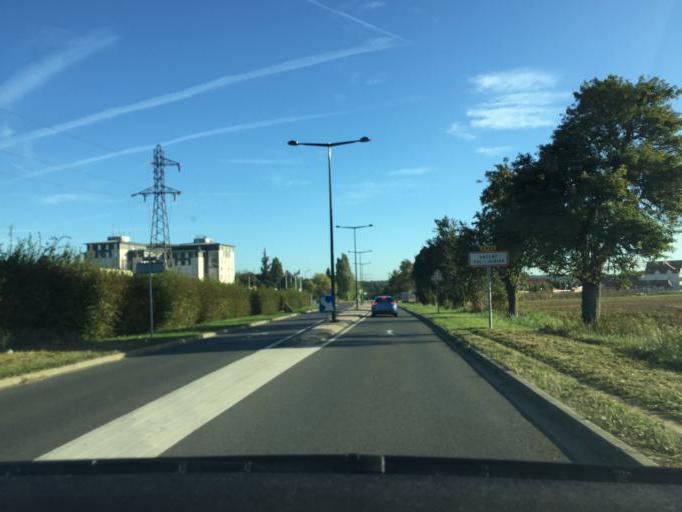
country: FR
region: Ile-de-France
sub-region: Departement des Yvelines
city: Jouy-en-Josas
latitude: 48.7540
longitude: 2.1698
